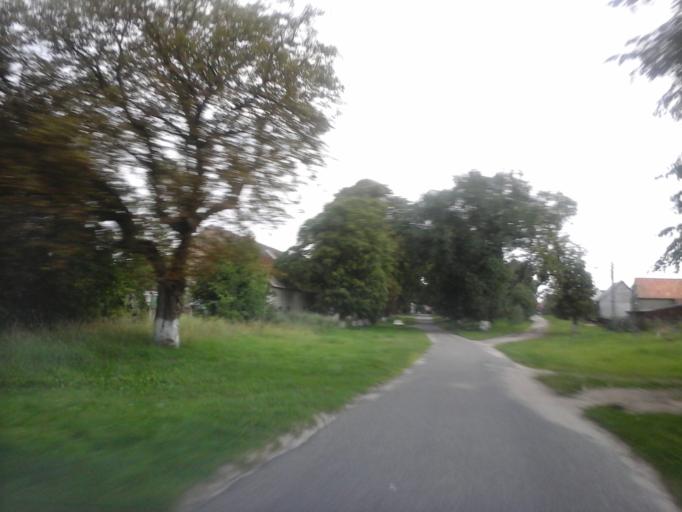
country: PL
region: West Pomeranian Voivodeship
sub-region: Powiat choszczenski
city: Recz
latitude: 53.2147
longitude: 15.4963
